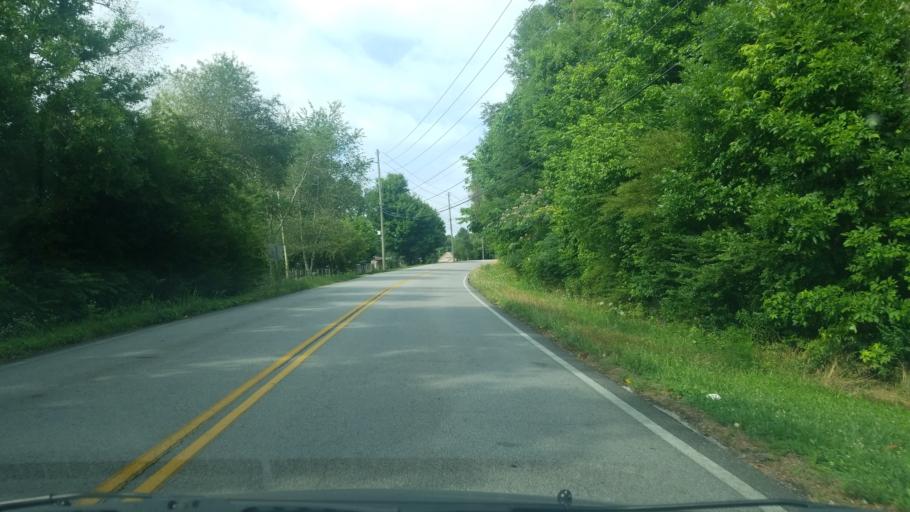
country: US
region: Tennessee
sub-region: Hamilton County
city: Apison
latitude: 35.0149
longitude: -85.0348
